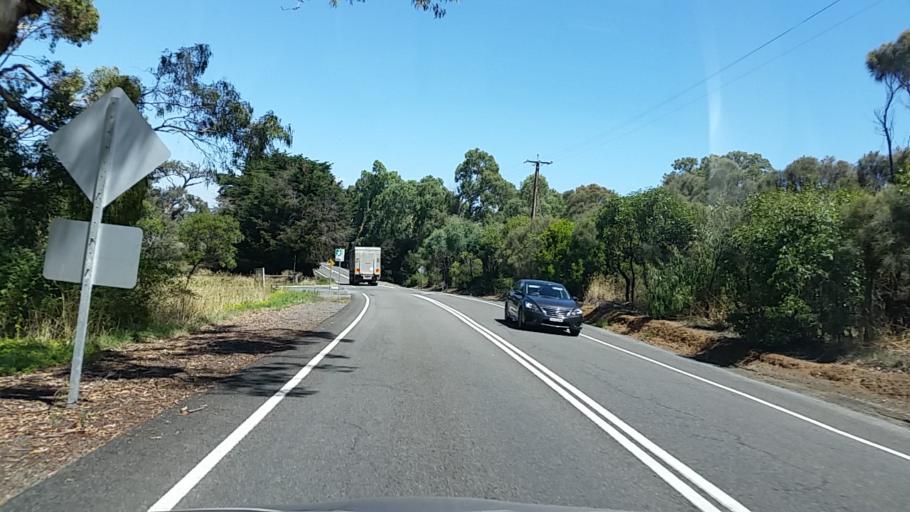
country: AU
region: South Australia
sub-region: Mount Barker
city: Little Hampton
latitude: -35.0303
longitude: 138.8611
